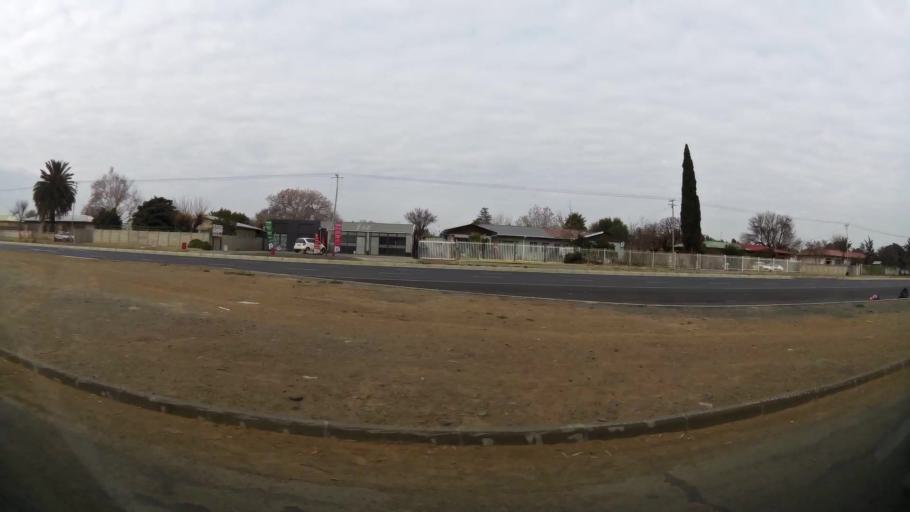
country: ZA
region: Orange Free State
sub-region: Mangaung Metropolitan Municipality
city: Bloemfontein
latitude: -29.1254
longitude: 26.1929
